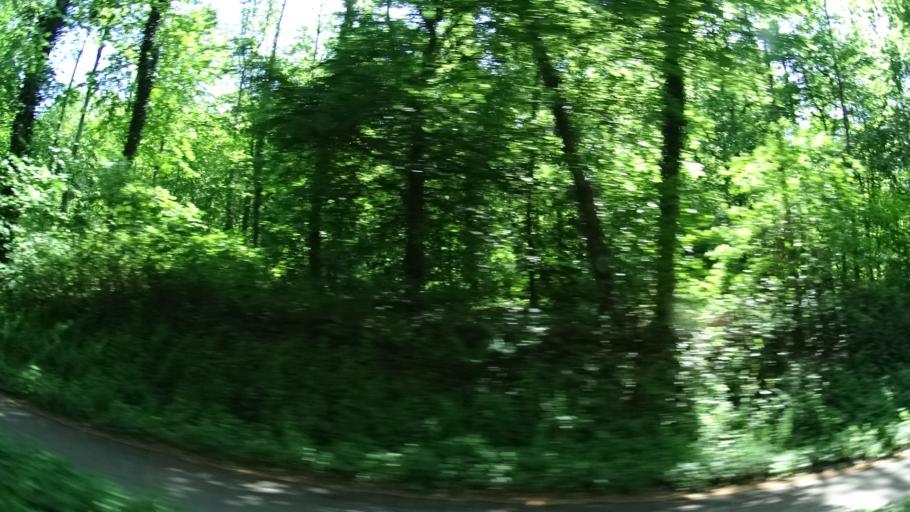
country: DE
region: Baden-Wuerttemberg
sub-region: Karlsruhe Region
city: Malsch
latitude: 48.9064
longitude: 8.3675
